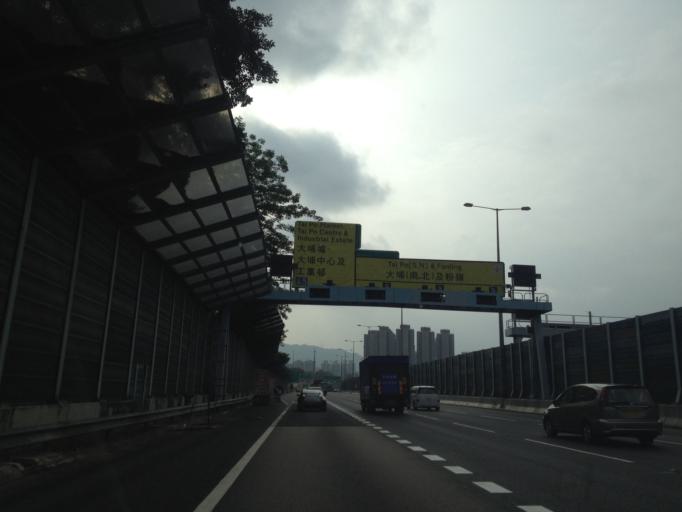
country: HK
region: Tai Po
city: Tai Po
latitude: 22.4414
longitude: 114.1829
